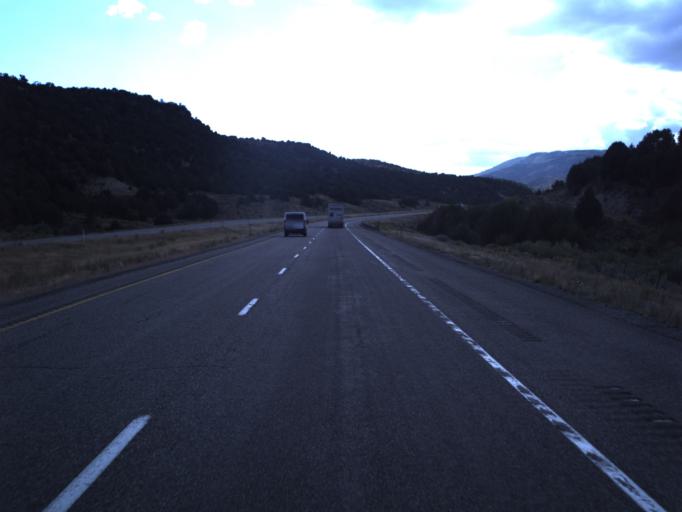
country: US
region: Utah
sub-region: Sevier County
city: Salina
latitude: 38.8430
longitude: -111.5389
